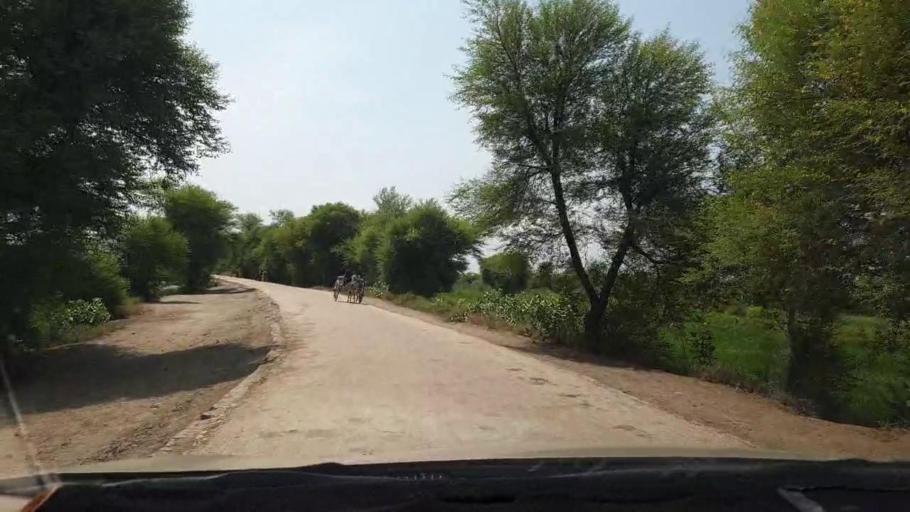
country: PK
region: Sindh
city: Larkana
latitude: 27.6264
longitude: 68.2732
